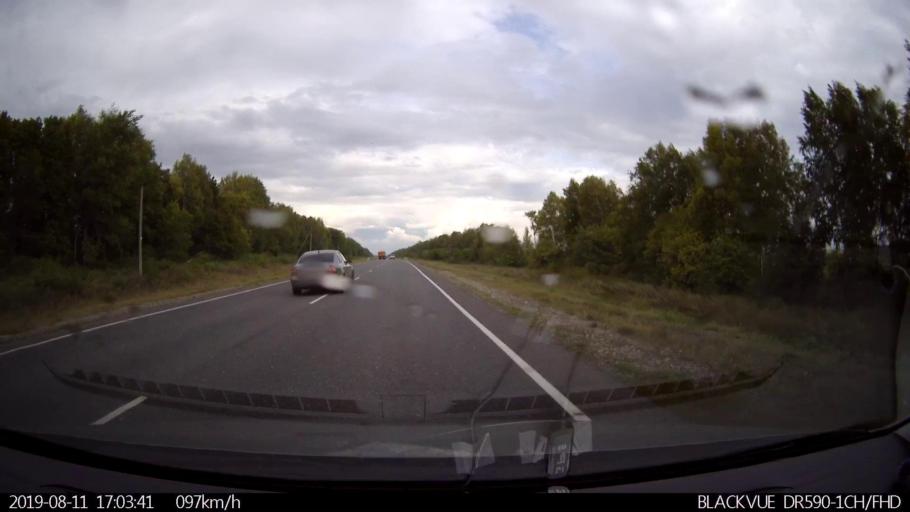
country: RU
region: Ulyanovsk
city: Mayna
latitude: 54.3022
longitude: 47.7463
